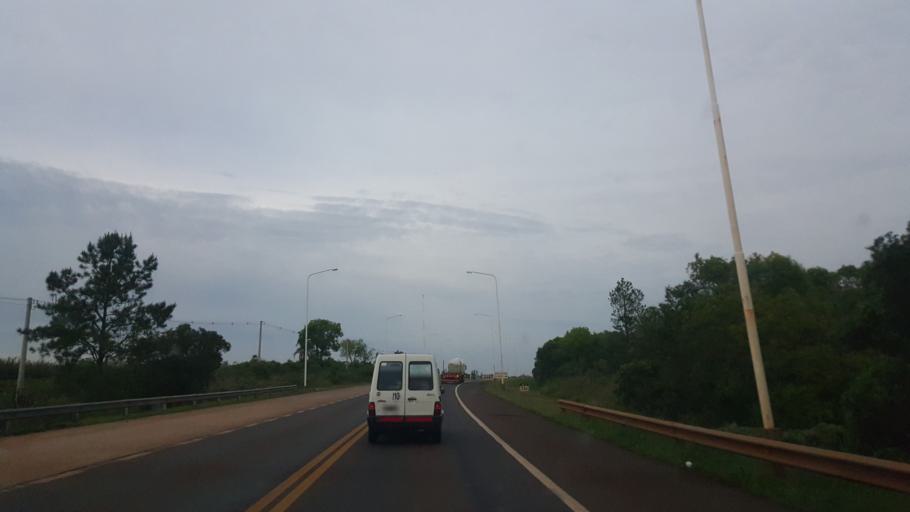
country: AR
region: Misiones
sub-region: Departamento de Apostoles
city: San Jose
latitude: -27.7795
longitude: -55.8126
